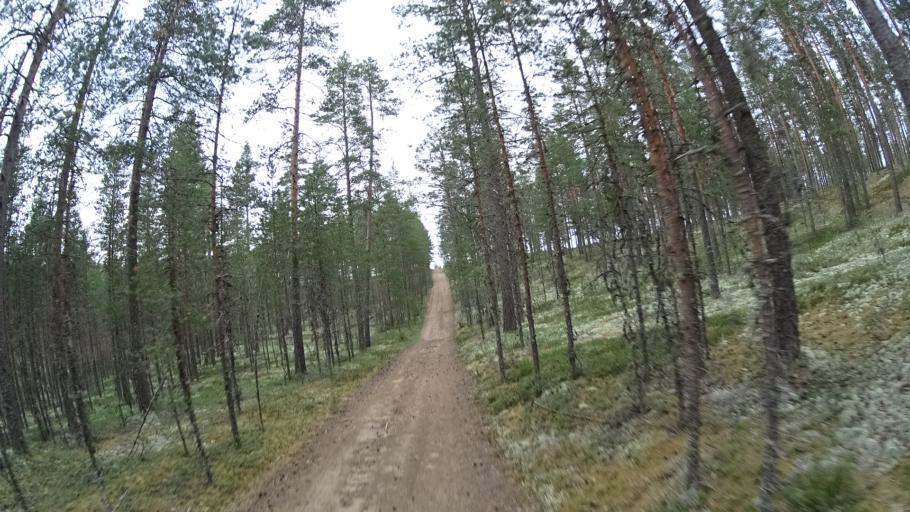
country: FI
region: Satakunta
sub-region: Pohjois-Satakunta
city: Jaemijaervi
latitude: 61.7685
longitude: 22.7905
